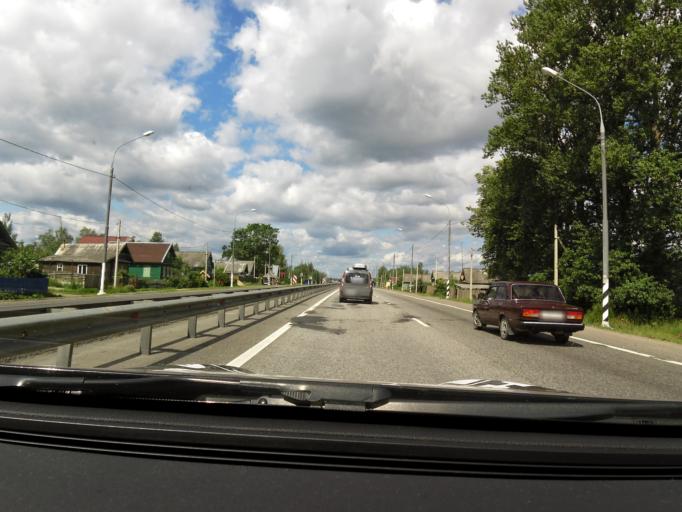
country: RU
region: Tverskaya
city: Torzhok
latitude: 56.9950
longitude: 35.1791
